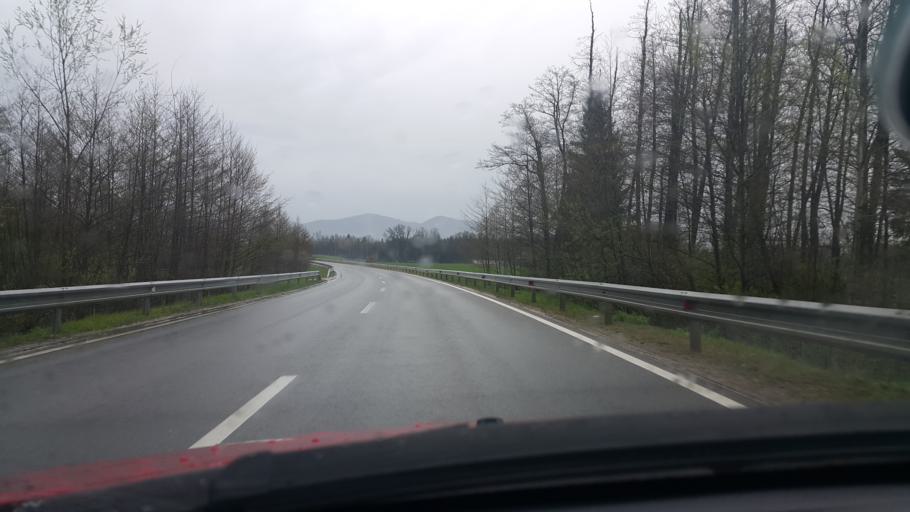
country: SI
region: Celje
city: Ljubecna
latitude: 46.2492
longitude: 15.3100
